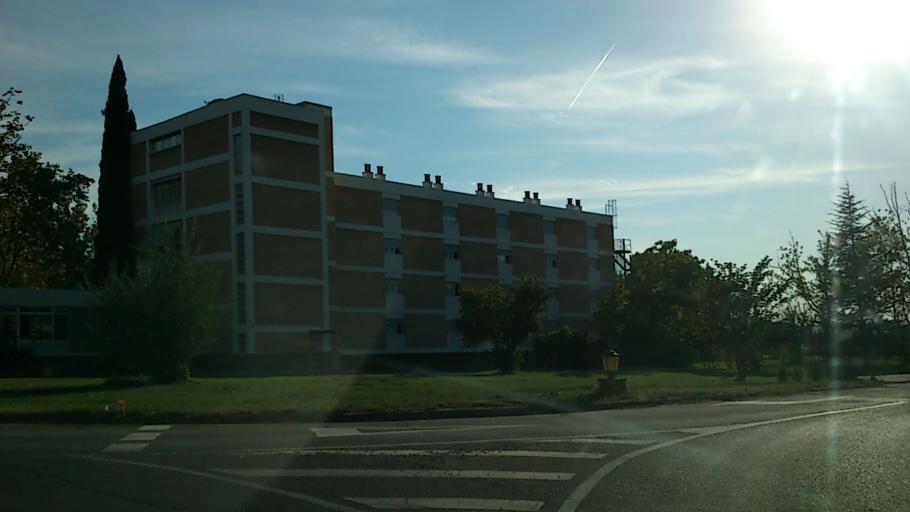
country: ES
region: Aragon
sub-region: Provincia de Zaragoza
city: Villanueva de Gallego
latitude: 41.7242
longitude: -0.8122
